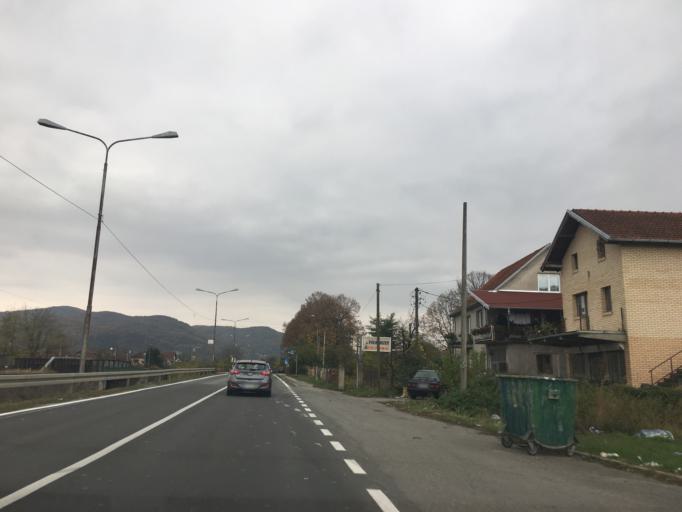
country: RS
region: Central Serbia
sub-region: Raski Okrug
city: Kraljevo
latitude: 43.7269
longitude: 20.7246
